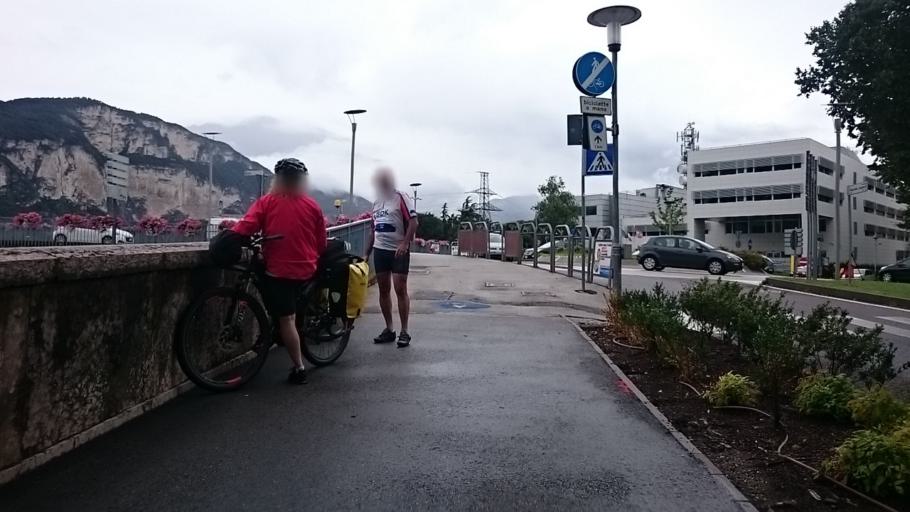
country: IT
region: Trentino-Alto Adige
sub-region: Provincia di Trento
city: Trento
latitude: 46.0773
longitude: 11.1161
